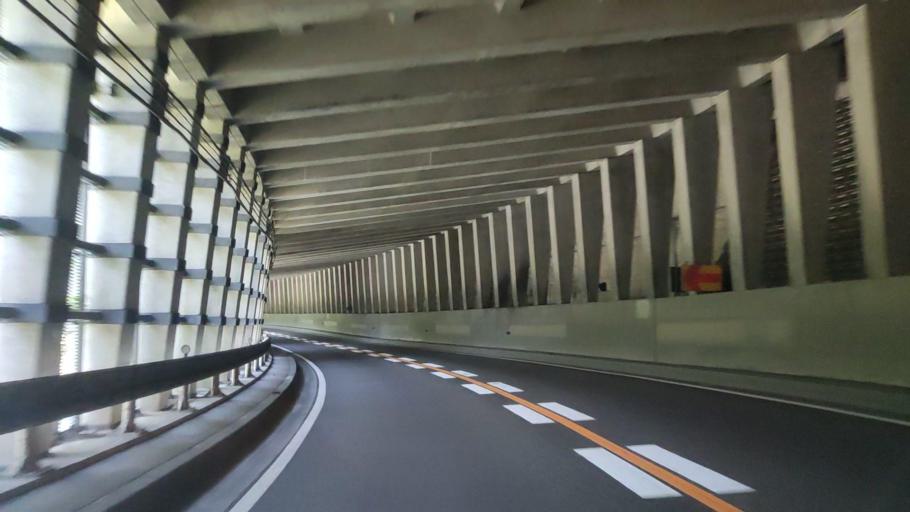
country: JP
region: Niigata
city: Itoigawa
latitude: 36.9076
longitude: 137.8615
